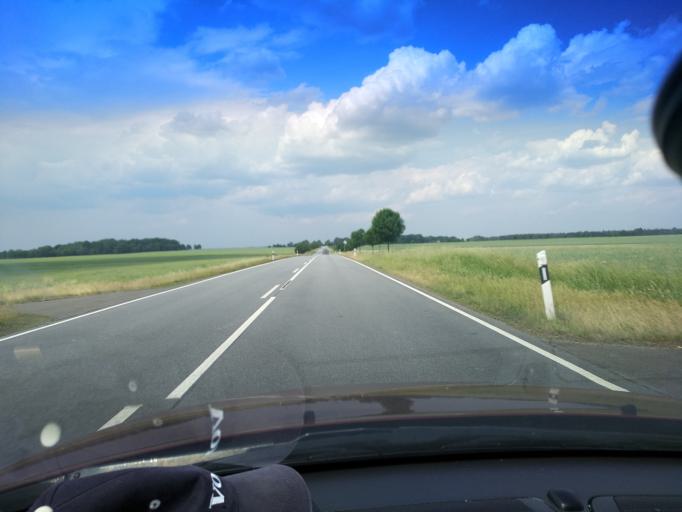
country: DE
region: Saxony
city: Kodersdorf
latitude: 51.2571
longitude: 14.8697
